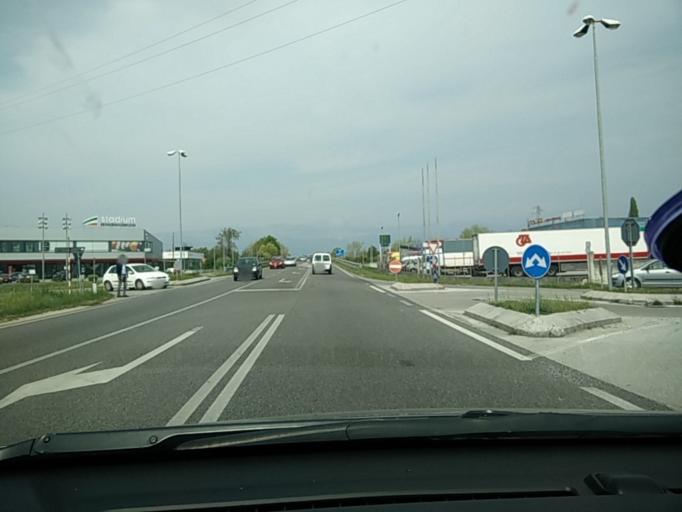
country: IT
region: Friuli Venezia Giulia
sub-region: Provincia di Pordenone
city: Pordenone
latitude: 45.9534
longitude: 12.6862
